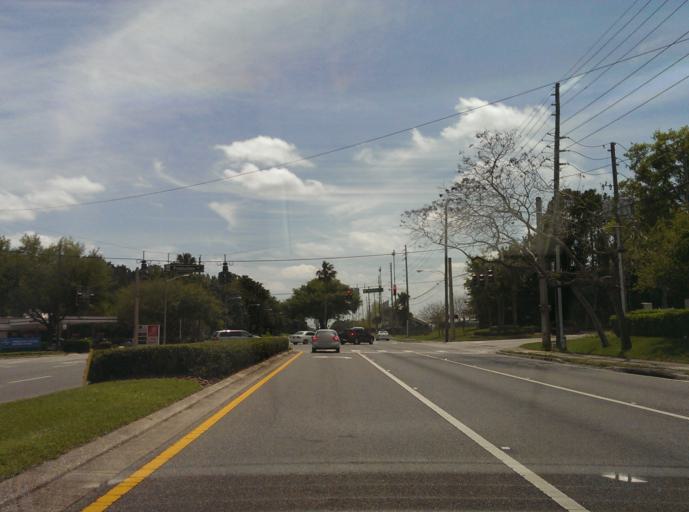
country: US
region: Florida
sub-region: Orange County
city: Doctor Phillips
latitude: 28.4759
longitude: -81.4750
